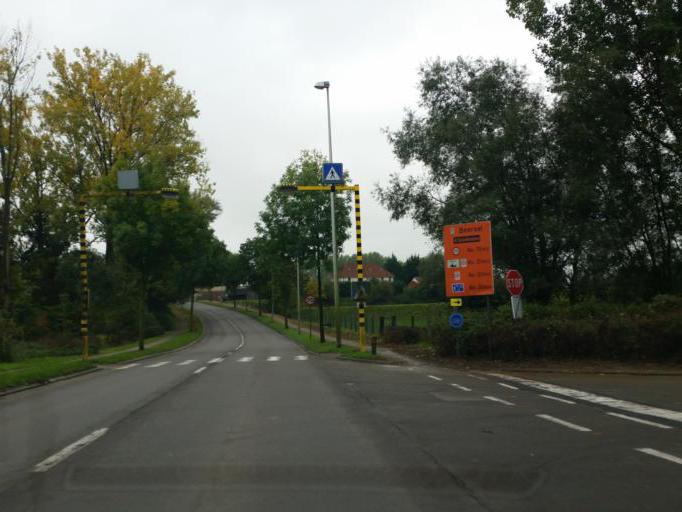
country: BE
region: Flanders
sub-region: Provincie Vlaams-Brabant
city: Sint-Pieters-Leeuw
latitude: 50.7688
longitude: 4.2686
